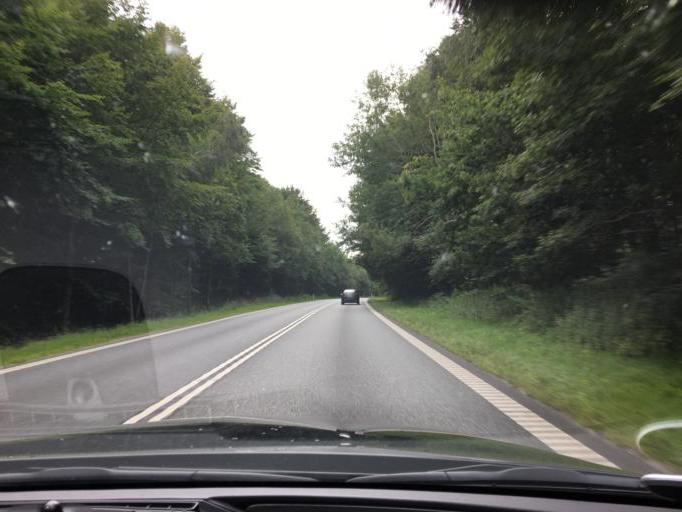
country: DK
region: Capital Region
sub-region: Hillerod Kommune
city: Hillerod
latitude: 55.9530
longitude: 12.3057
